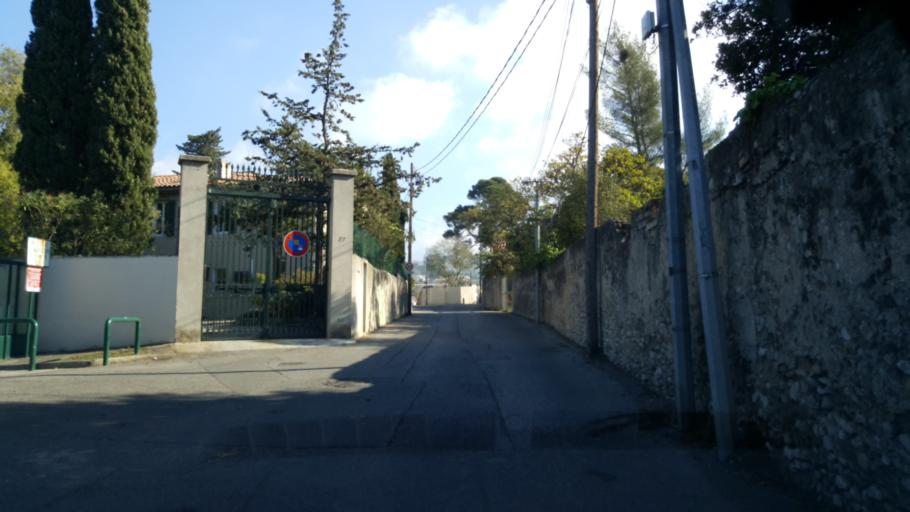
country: FR
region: Provence-Alpes-Cote d'Azur
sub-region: Departement des Bouches-du-Rhone
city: Marseille 09
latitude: 43.2651
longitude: 5.4141
